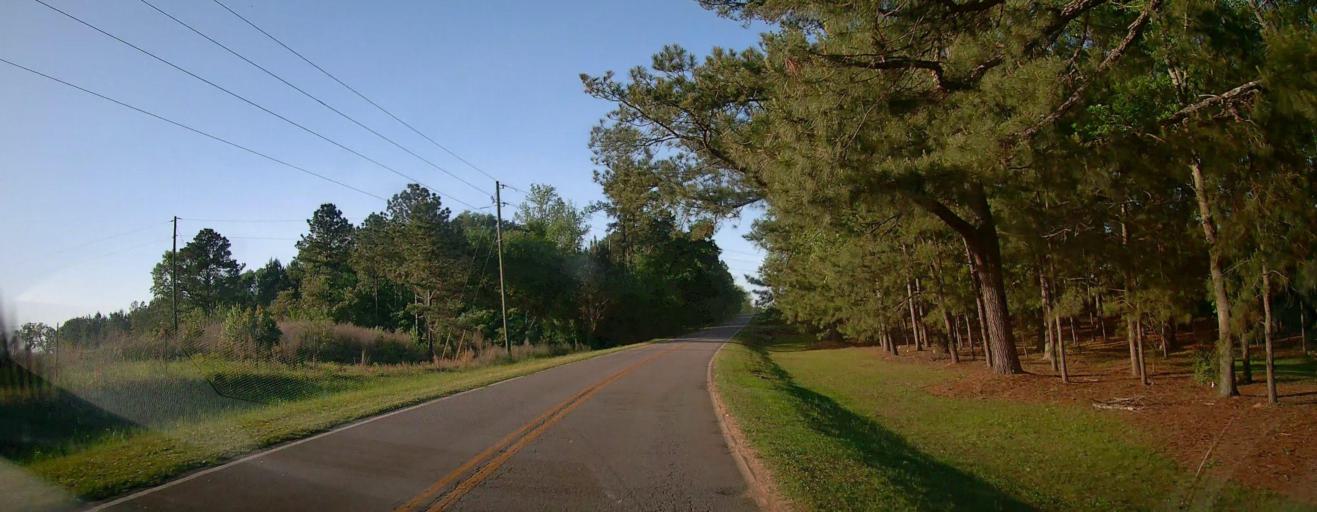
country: US
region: Georgia
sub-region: Macon County
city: Oglethorpe
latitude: 32.2795
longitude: -84.0910
